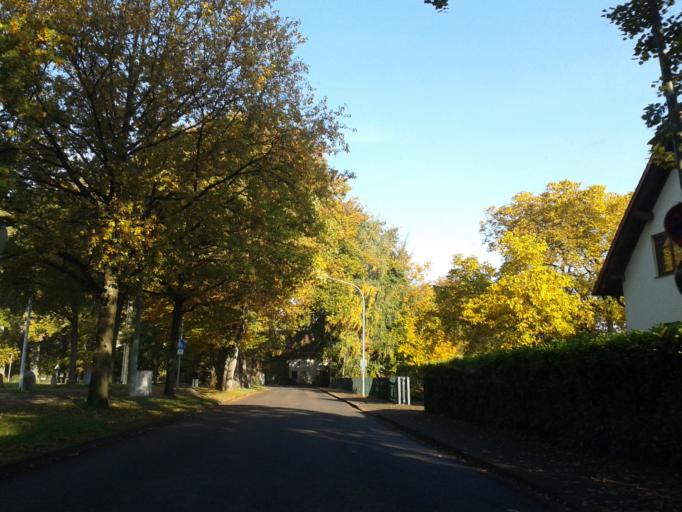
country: DE
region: North Rhine-Westphalia
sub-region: Regierungsbezirk Detmold
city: Paderborn
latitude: 51.7376
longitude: 8.6882
